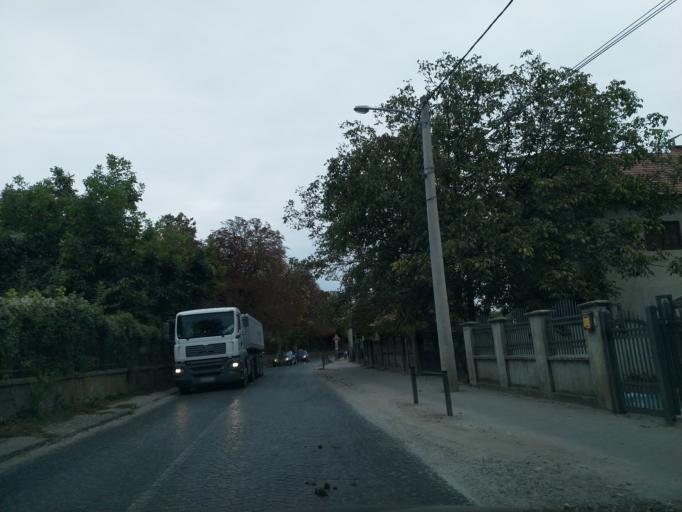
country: RS
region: Central Serbia
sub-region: Pomoravski Okrug
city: Paracin
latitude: 43.8573
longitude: 21.4007
